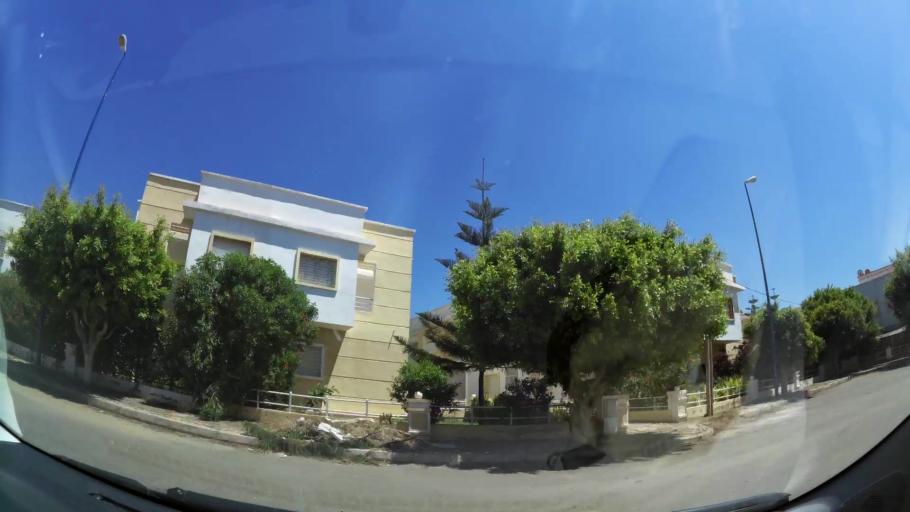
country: MA
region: Oriental
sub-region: Berkane-Taourirt
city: Madagh
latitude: 35.0730
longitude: -2.2164
